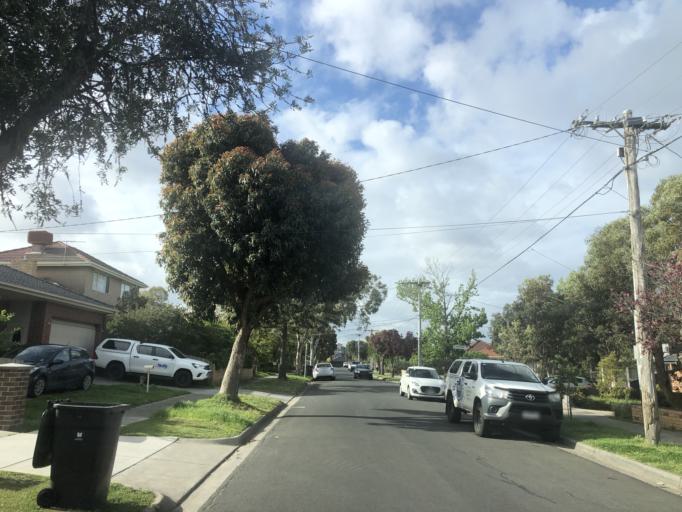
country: AU
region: Victoria
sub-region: Monash
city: Ashwood
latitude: -37.8817
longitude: 145.1160
